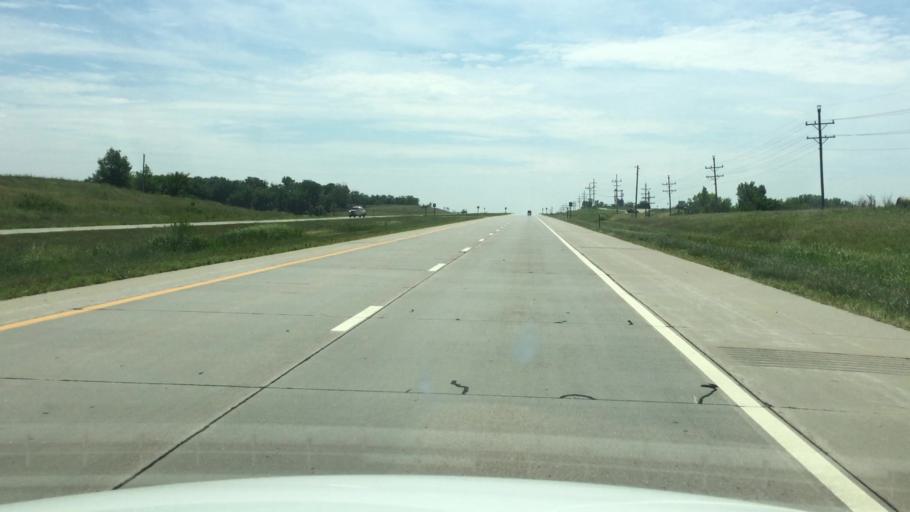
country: US
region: Kansas
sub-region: Jackson County
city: Holton
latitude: 39.3000
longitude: -95.7195
